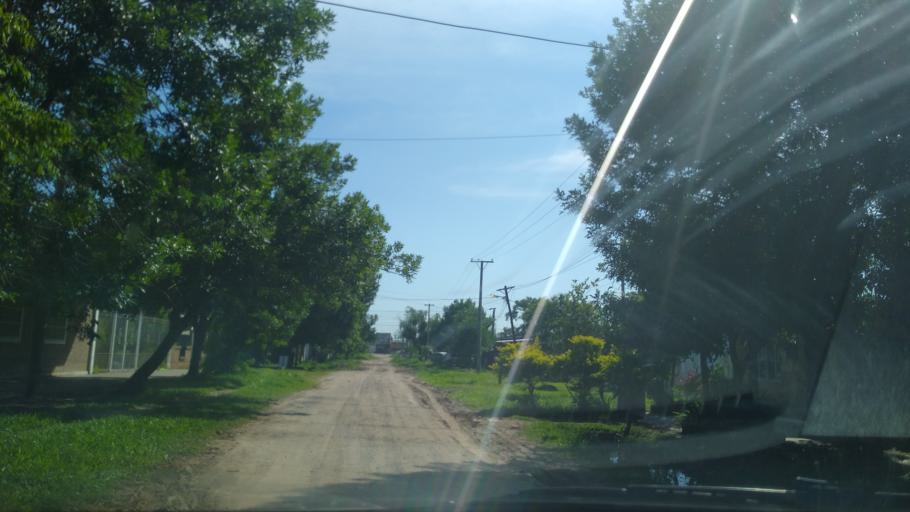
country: AR
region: Chaco
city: Barranqueras
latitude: -27.4888
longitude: -58.9549
